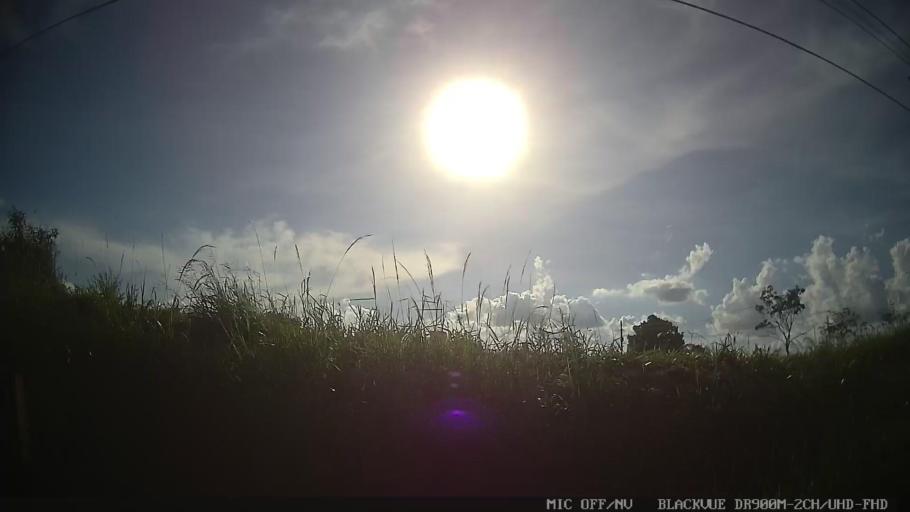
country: BR
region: Sao Paulo
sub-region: Tiete
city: Tiete
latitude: -23.0931
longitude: -47.7790
